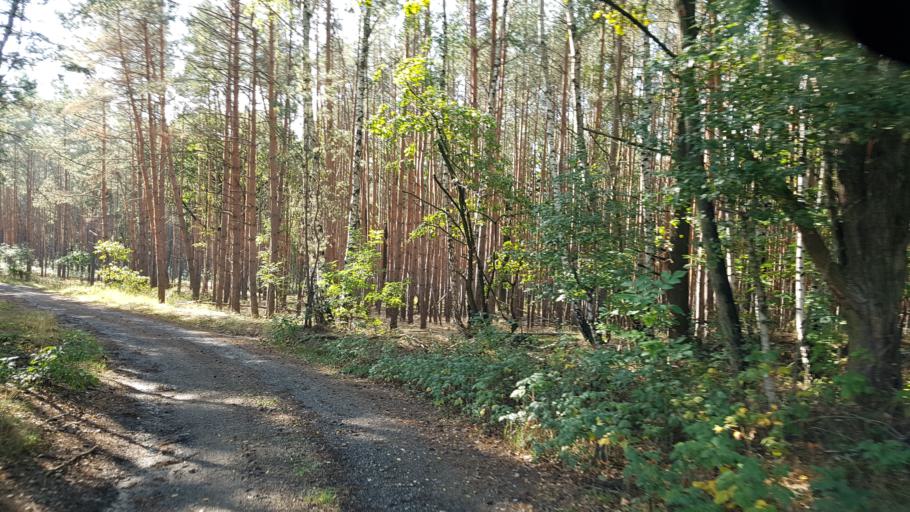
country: DE
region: Brandenburg
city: Plessa
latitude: 51.5279
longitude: 13.6362
